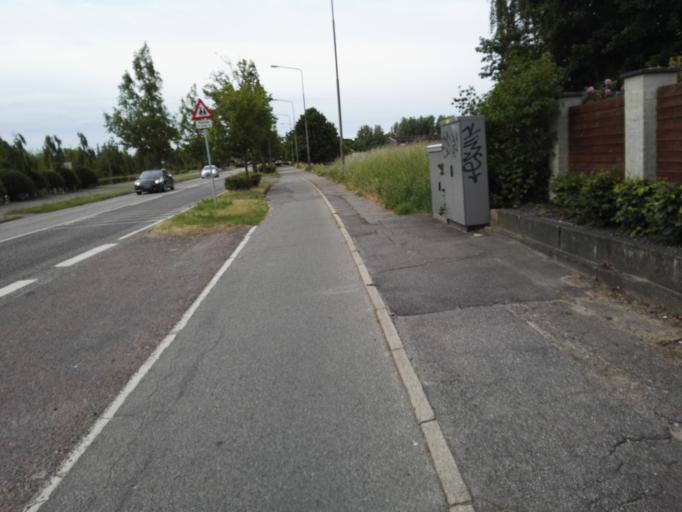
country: DK
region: Capital Region
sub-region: Ballerup Kommune
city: Ballerup
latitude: 55.7449
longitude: 12.3673
